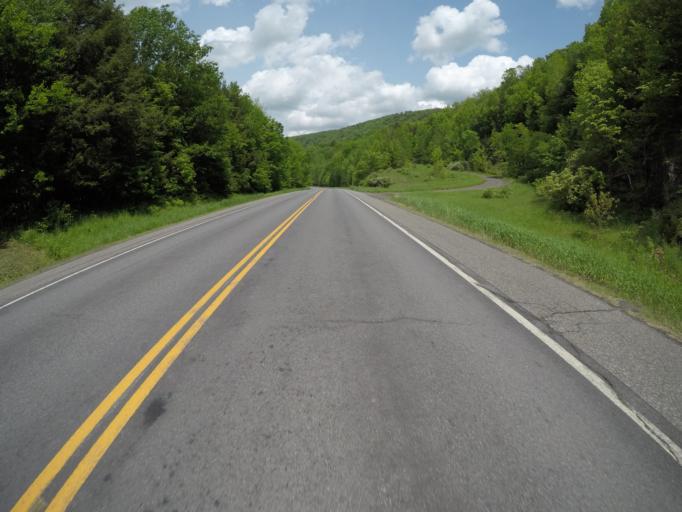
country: US
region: New York
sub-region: Delaware County
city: Stamford
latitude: 42.2094
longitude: -74.5968
